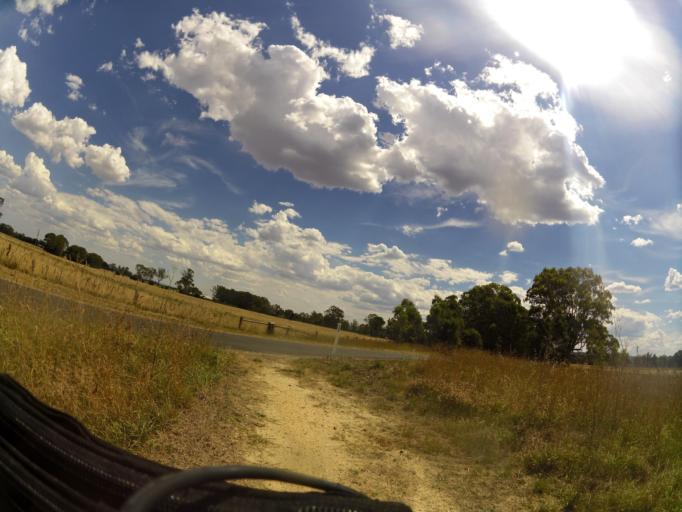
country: AU
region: Victoria
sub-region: Wellington
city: Heyfield
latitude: -37.9840
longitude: 146.7226
